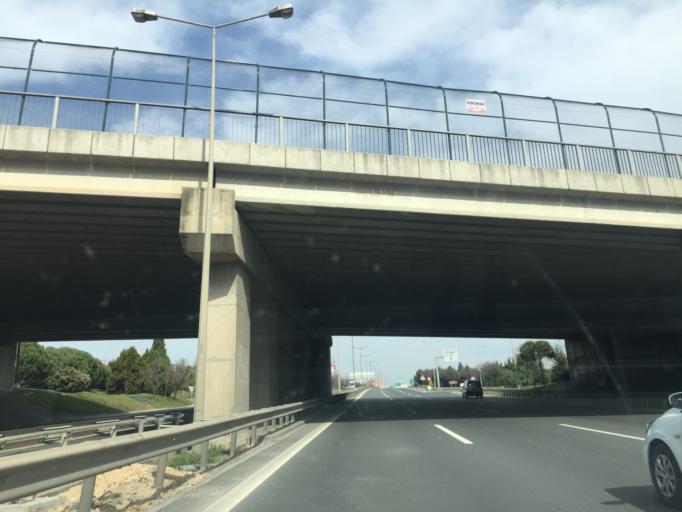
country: TR
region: Kocaeli
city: Balcik
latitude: 40.8630
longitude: 29.3831
